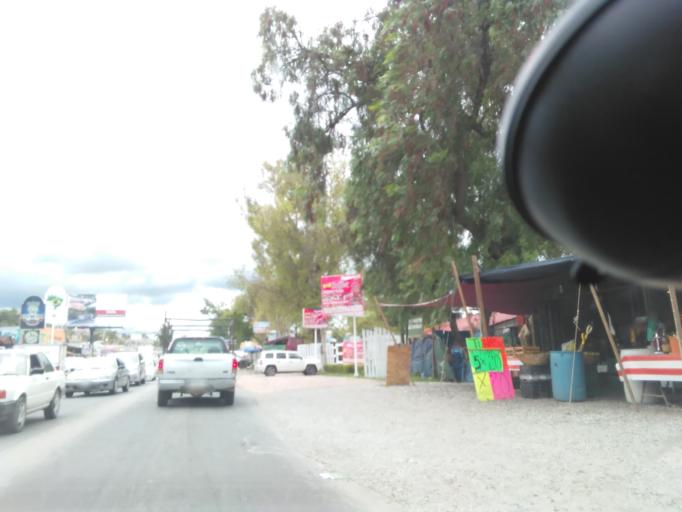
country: MX
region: Hidalgo
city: El Llano
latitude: 20.0566
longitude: -99.3266
